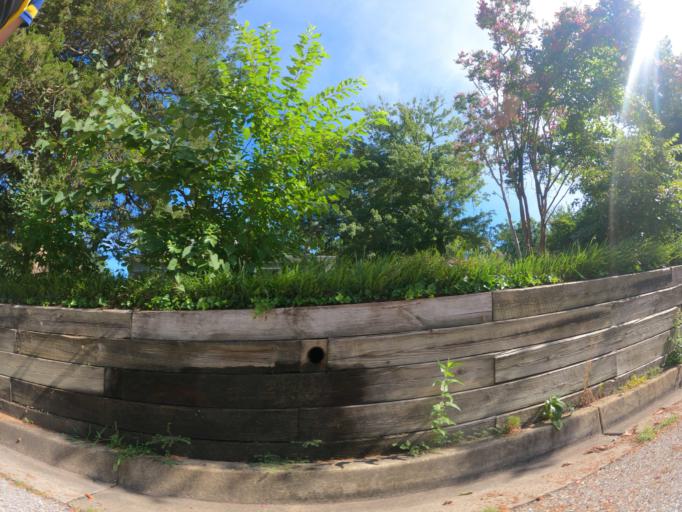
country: US
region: Maryland
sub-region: Howard County
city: Savage
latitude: 39.1379
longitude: -76.8206
